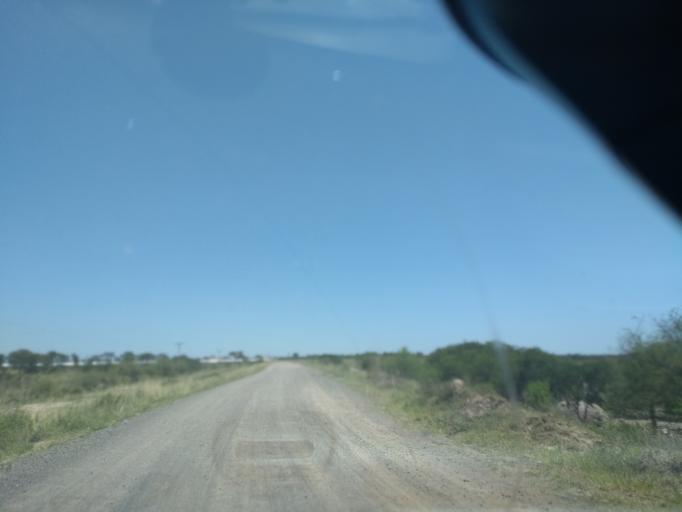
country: AR
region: Chaco
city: Resistencia
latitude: -27.4073
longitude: -58.9566
